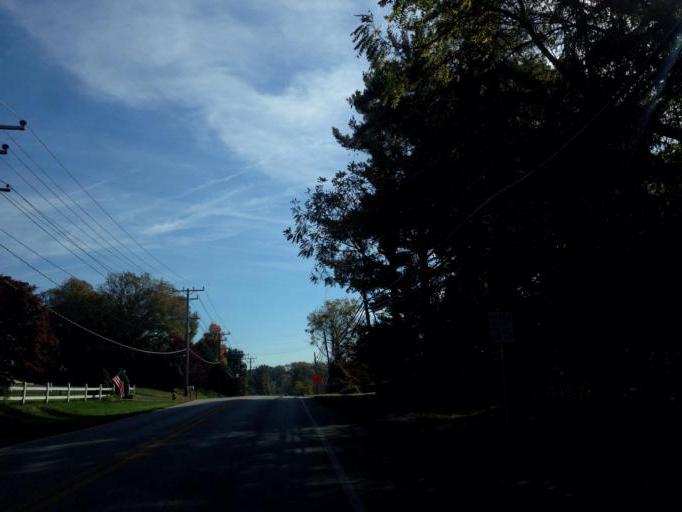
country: US
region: Maryland
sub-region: Howard County
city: Columbia
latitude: 39.2745
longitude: -76.8456
